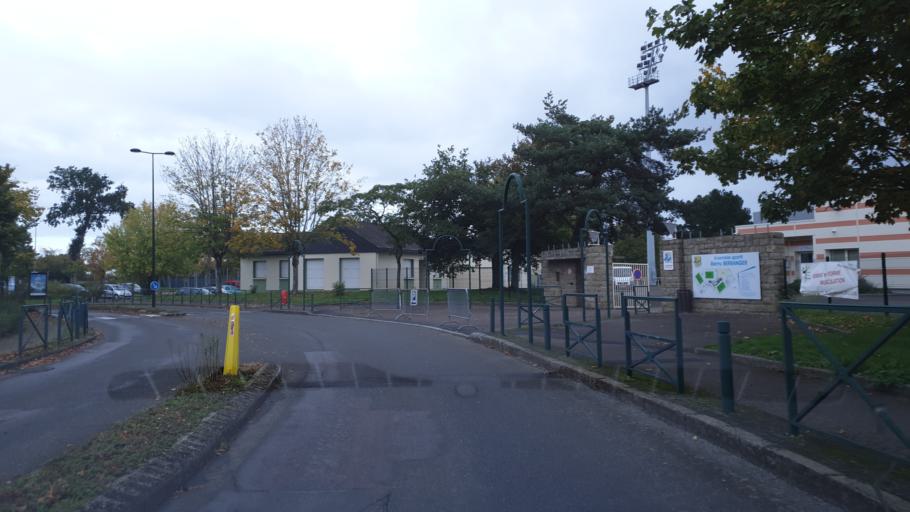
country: FR
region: Brittany
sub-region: Departement d'Ille-et-Vilaine
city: Chartres-de-Bretagne
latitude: 48.0461
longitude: -1.7064
